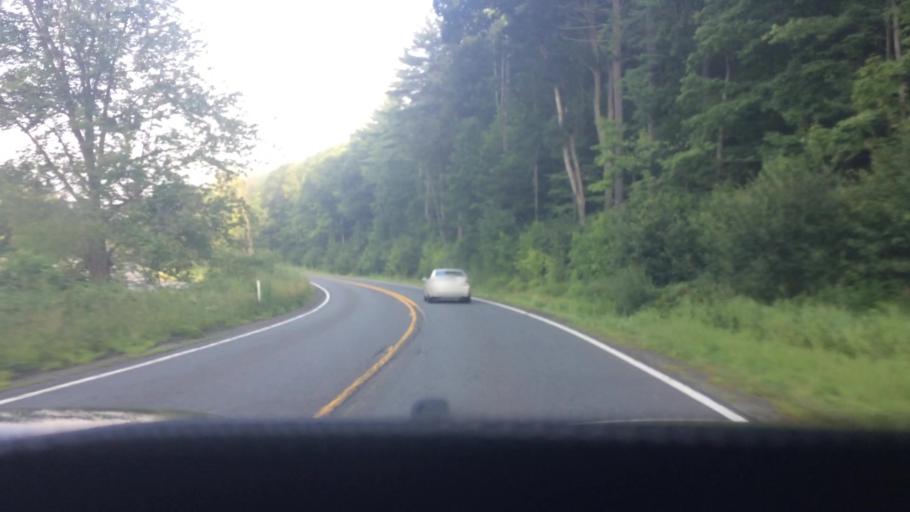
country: US
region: Massachusetts
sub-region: Franklin County
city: Erving
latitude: 42.6080
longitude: -72.4159
